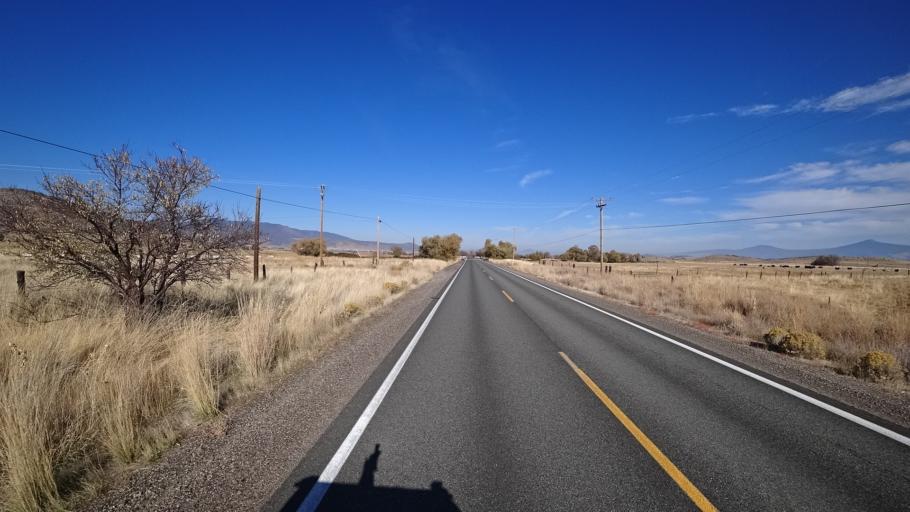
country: US
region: California
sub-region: Siskiyou County
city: Weed
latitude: 41.5070
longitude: -122.5169
